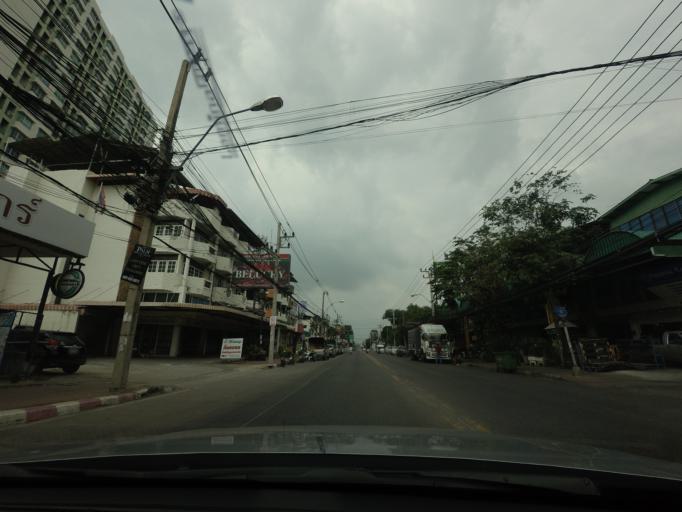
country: TH
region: Chon Buri
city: Phatthaya
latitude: 12.9580
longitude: 100.8925
